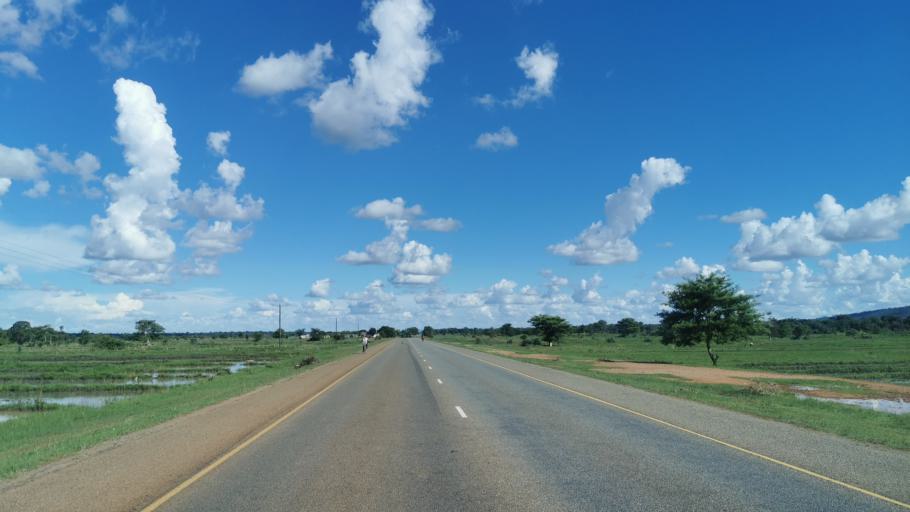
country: TZ
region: Geita
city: Ushirombo
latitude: -3.4801
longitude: 31.9231
